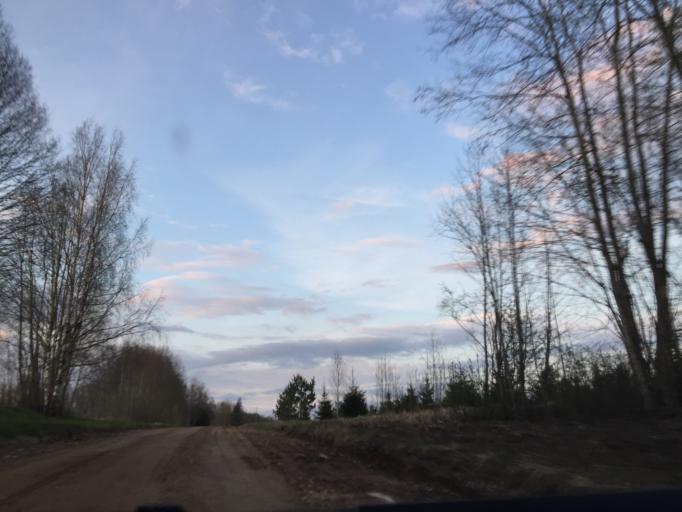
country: LV
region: Aluksnes Rajons
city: Aluksne
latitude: 57.3130
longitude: 26.9172
